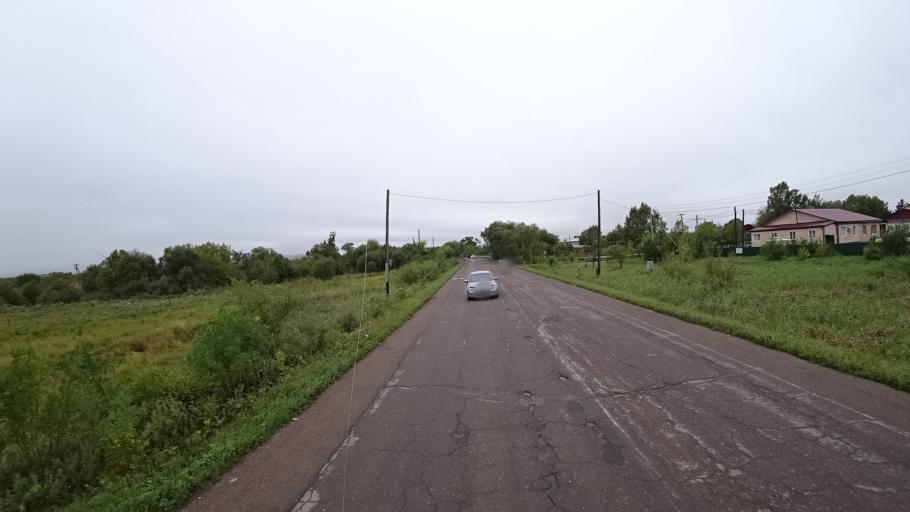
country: RU
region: Primorskiy
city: Monastyrishche
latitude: 44.2026
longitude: 132.4310
